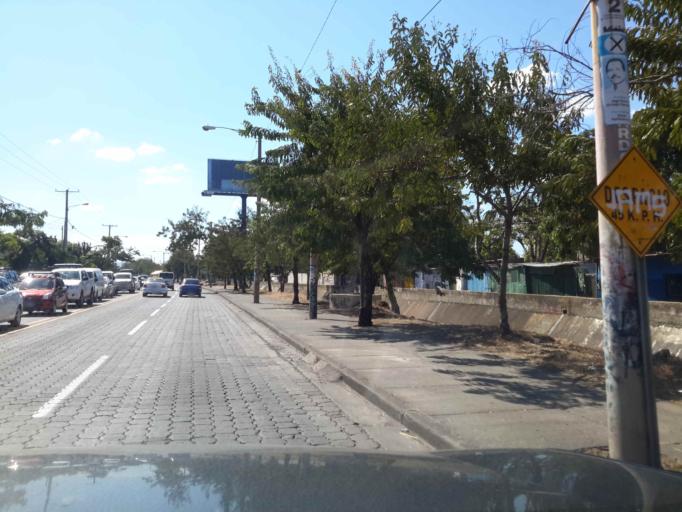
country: NI
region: Managua
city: Managua
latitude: 12.1391
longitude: -86.2475
